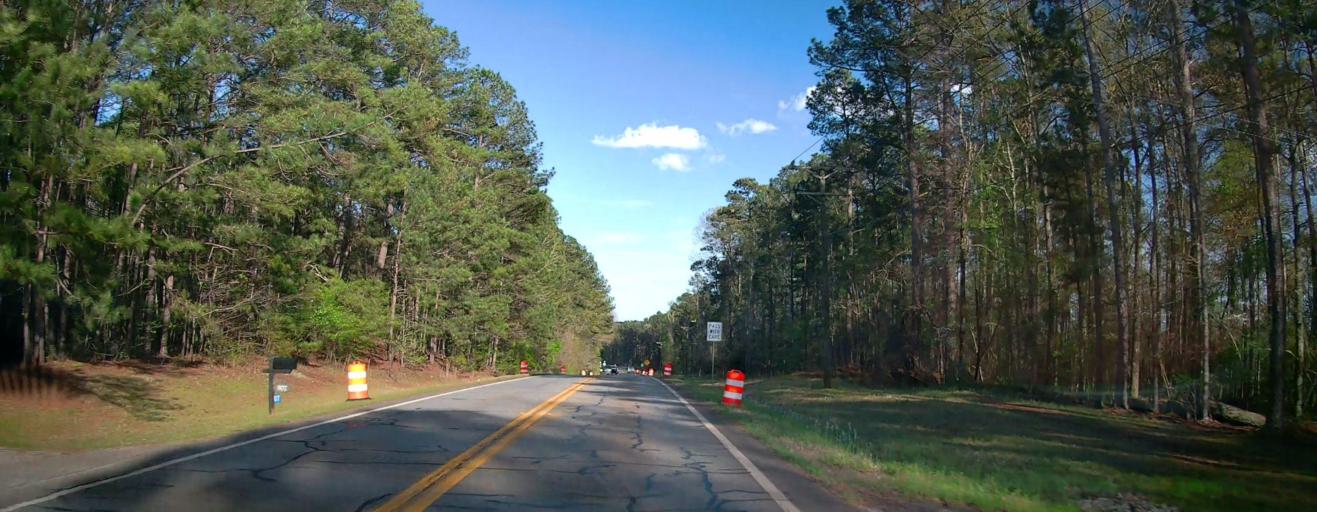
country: US
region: Georgia
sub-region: Baldwin County
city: Milledgeville
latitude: 33.1599
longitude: -83.3661
